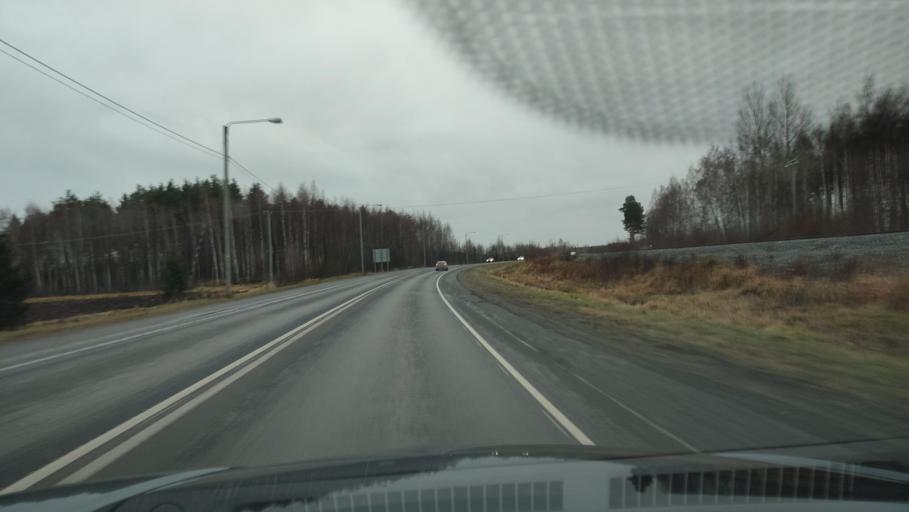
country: FI
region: Southern Ostrobothnia
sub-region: Seinaejoki
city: Ilmajoki
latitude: 62.7582
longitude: 22.6642
